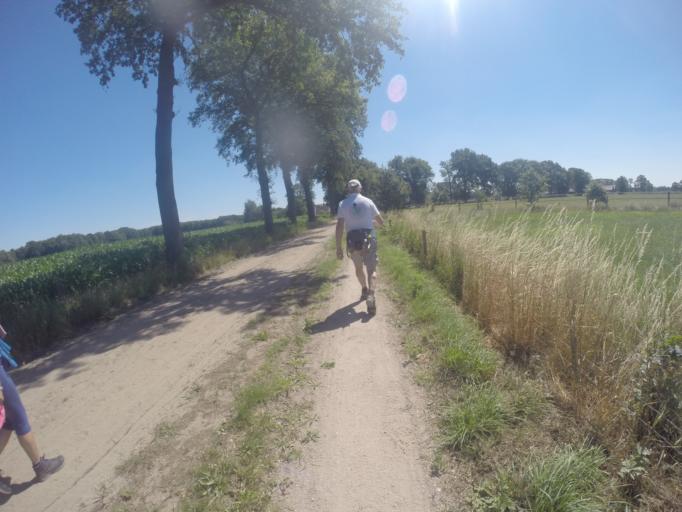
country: NL
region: Gelderland
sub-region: Gemeente Lochem
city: Lochem
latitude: 52.1343
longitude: 6.4131
